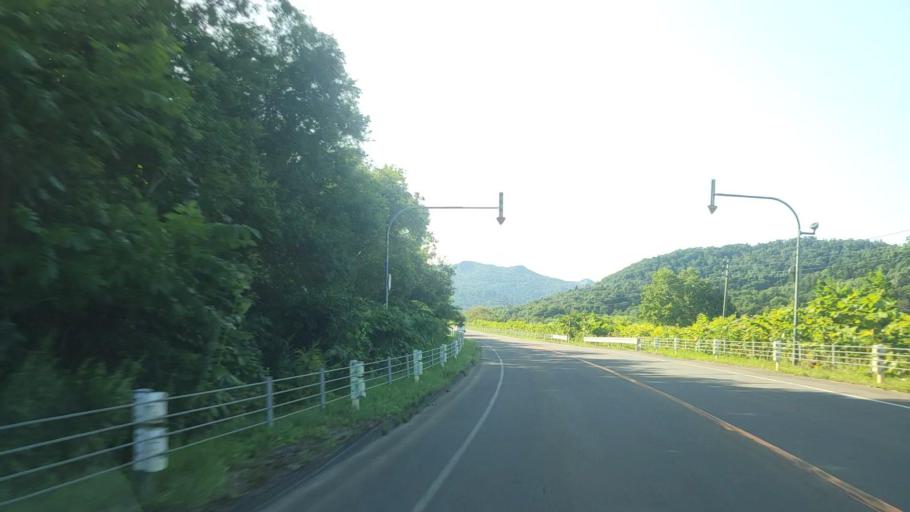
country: JP
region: Hokkaido
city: Nayoro
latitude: 44.7288
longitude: 142.2128
